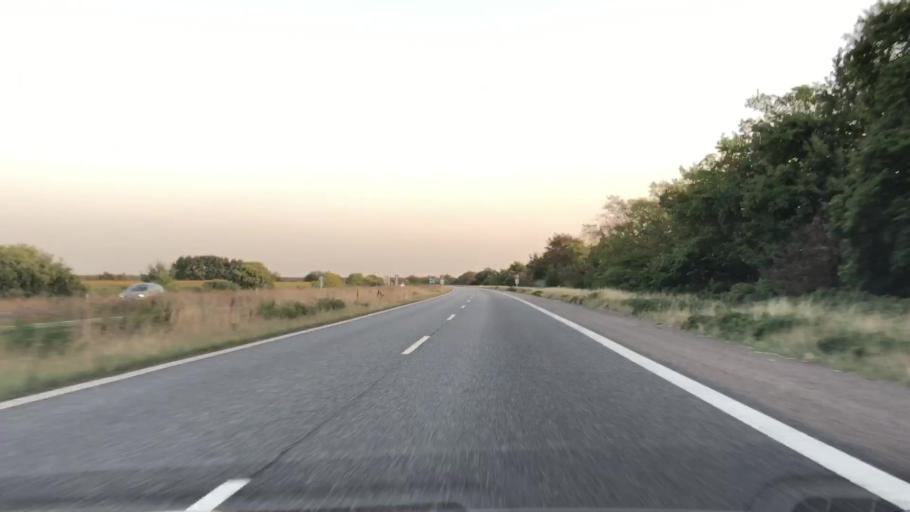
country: DK
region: South Denmark
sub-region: Aabenraa Kommune
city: Krusa
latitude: 54.9018
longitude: 9.3775
